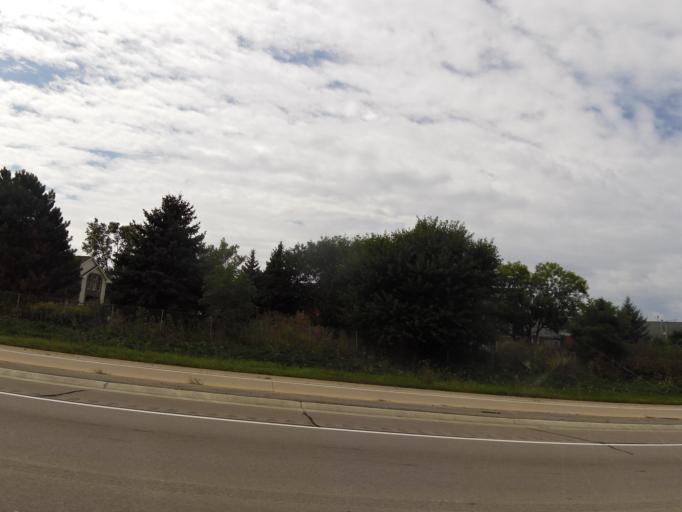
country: US
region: Wisconsin
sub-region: Dane County
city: Maple Bluff
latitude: 43.1415
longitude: -89.2992
